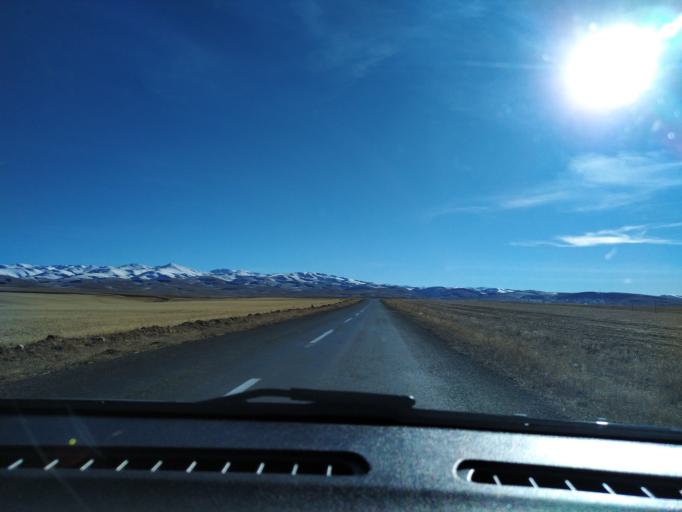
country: TR
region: Kayseri
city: Orensehir
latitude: 38.8922
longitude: 36.7293
